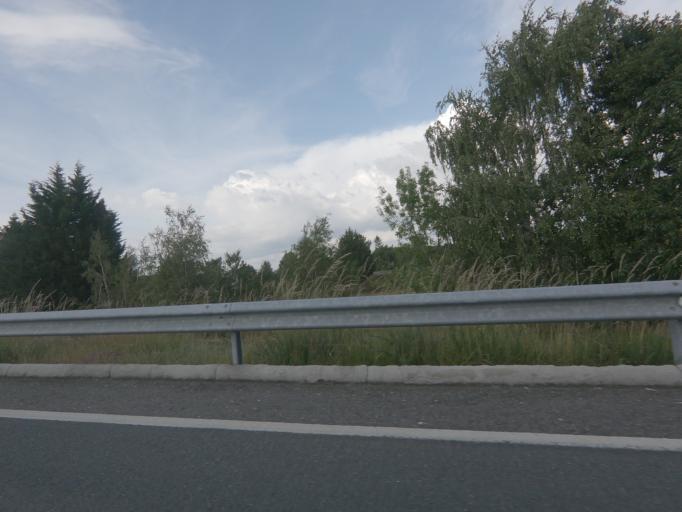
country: ES
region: Galicia
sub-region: Provincia de Ourense
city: Ambia
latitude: 42.1530
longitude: -7.7561
